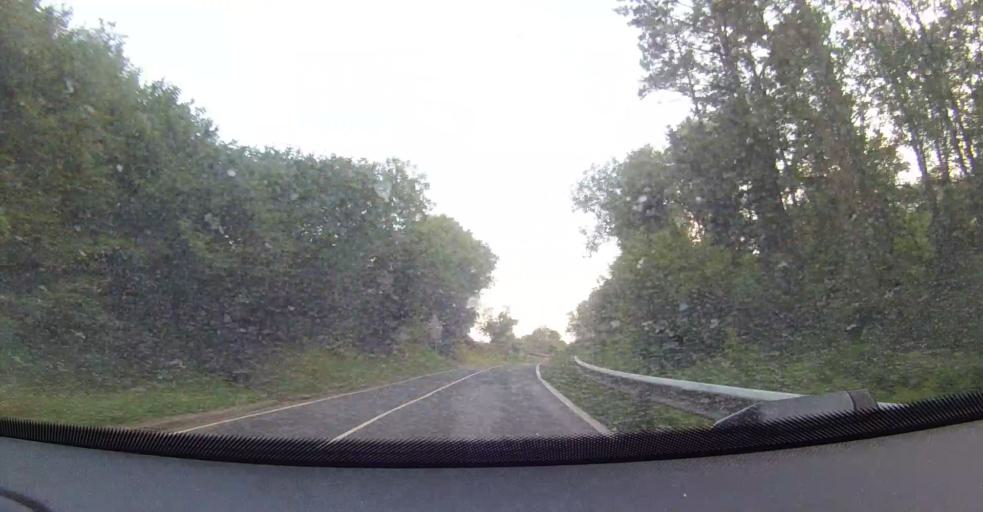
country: ES
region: Basque Country
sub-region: Bizkaia
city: Urrestieta
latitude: 43.2354
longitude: -3.1581
